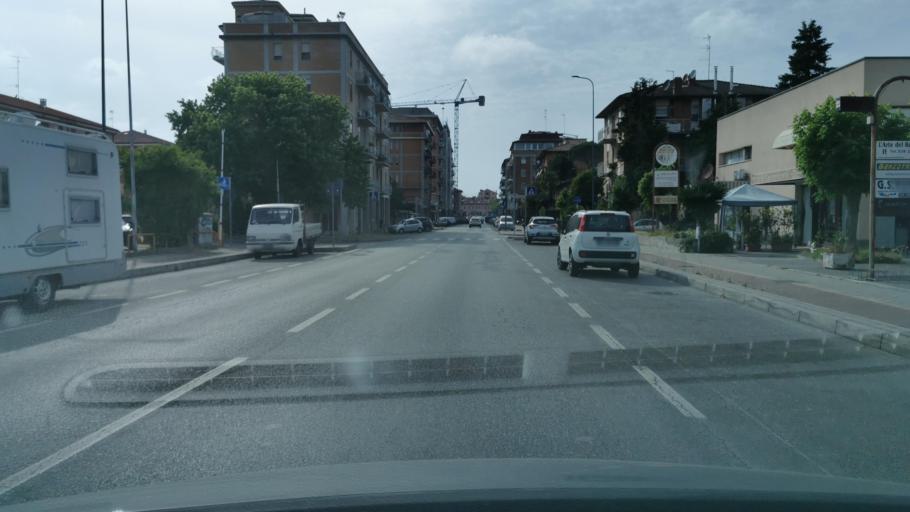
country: IT
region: Emilia-Romagna
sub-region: Provincia di Ravenna
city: Ravenna
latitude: 44.4049
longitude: 12.2038
